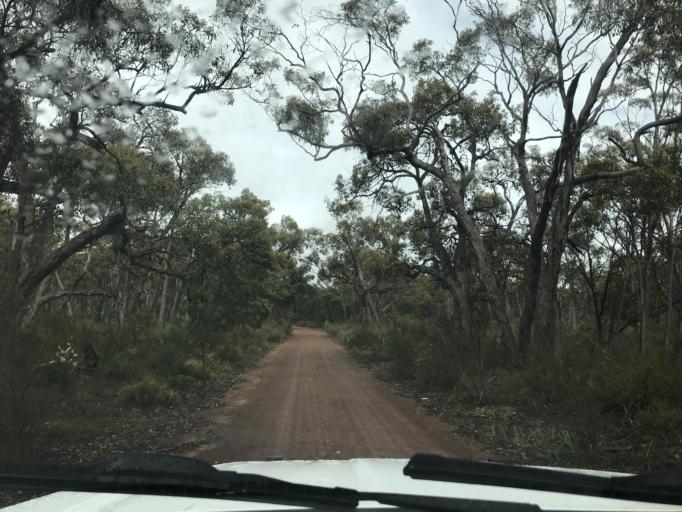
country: AU
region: South Australia
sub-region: Wattle Range
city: Penola
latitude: -37.2595
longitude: 141.3343
